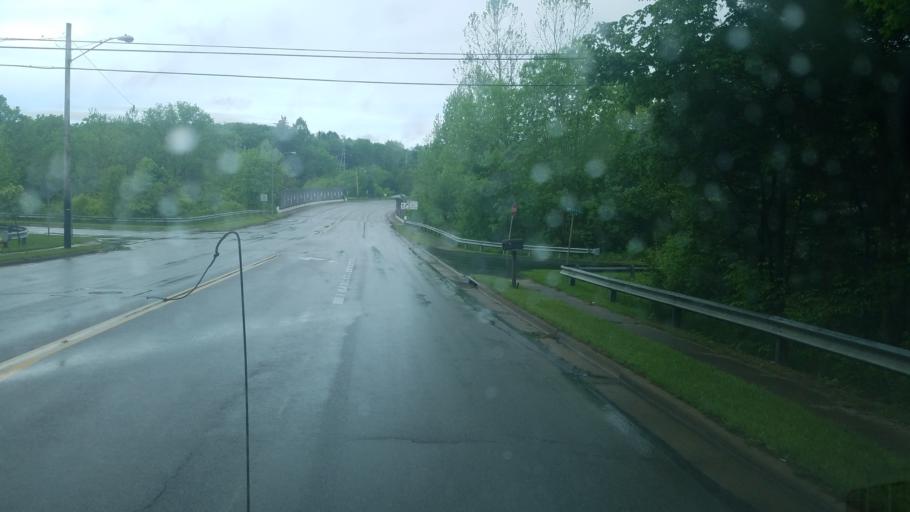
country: US
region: Ohio
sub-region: Wayne County
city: Wooster
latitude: 40.8269
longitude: -81.9211
